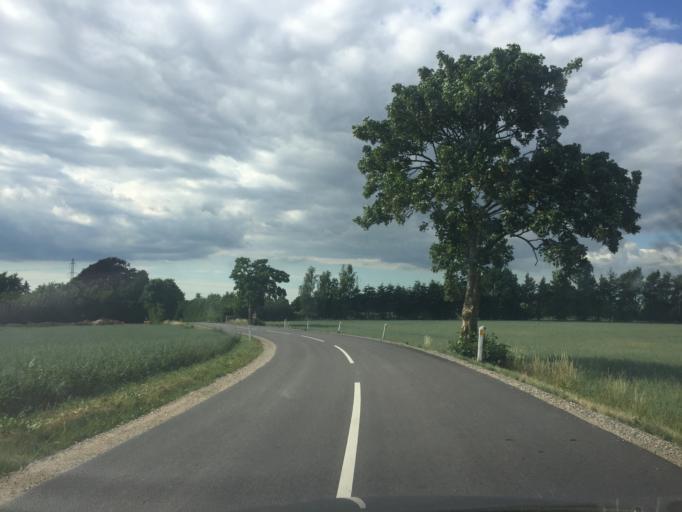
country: DK
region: Capital Region
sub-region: Egedal Kommune
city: Vekso
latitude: 55.7037
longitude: 12.2298
